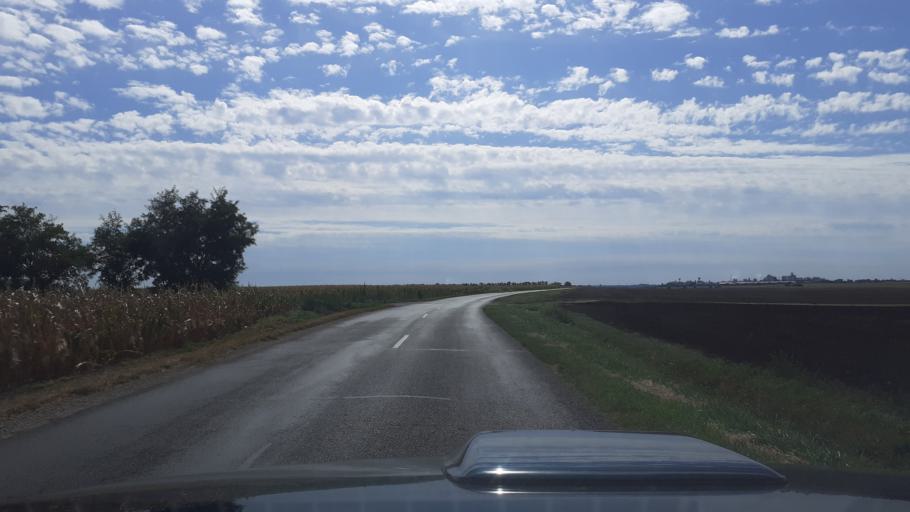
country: HU
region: Fejer
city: Pusztaszabolcs
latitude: 47.1130
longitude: 18.7021
